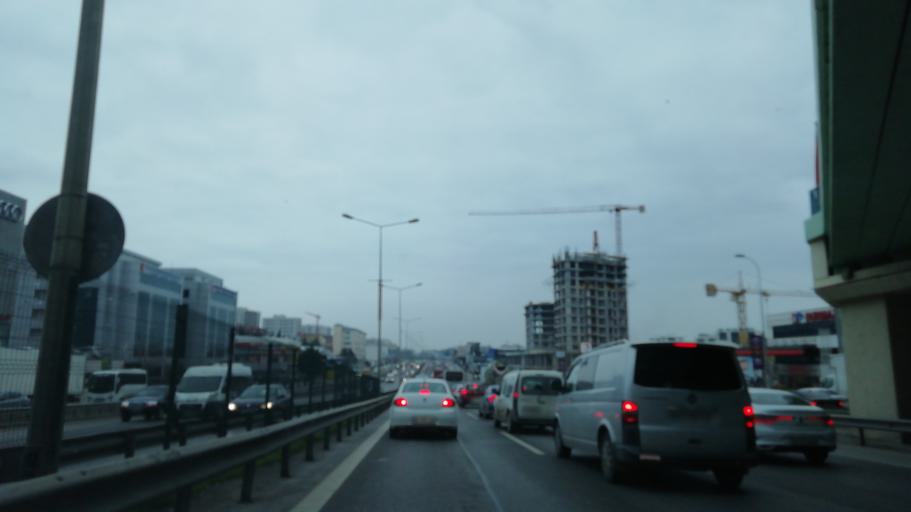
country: TR
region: Istanbul
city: Pendik
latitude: 40.8951
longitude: 29.2280
